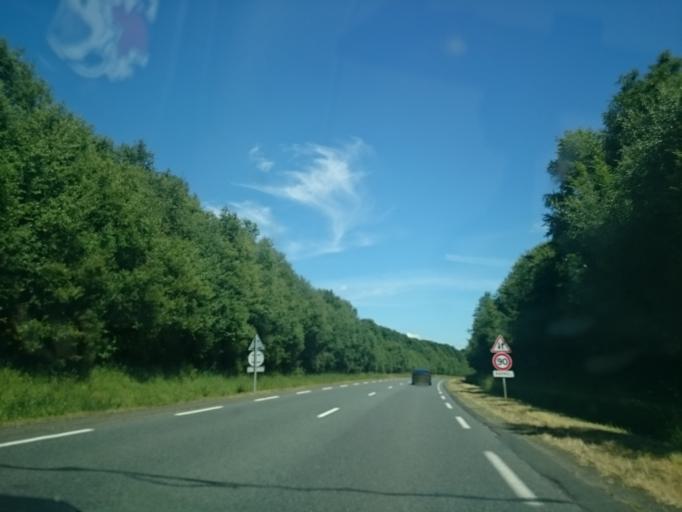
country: FR
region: Brittany
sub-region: Departement des Cotes-d'Armor
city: Plouguernevel
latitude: 48.2443
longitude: -3.2402
